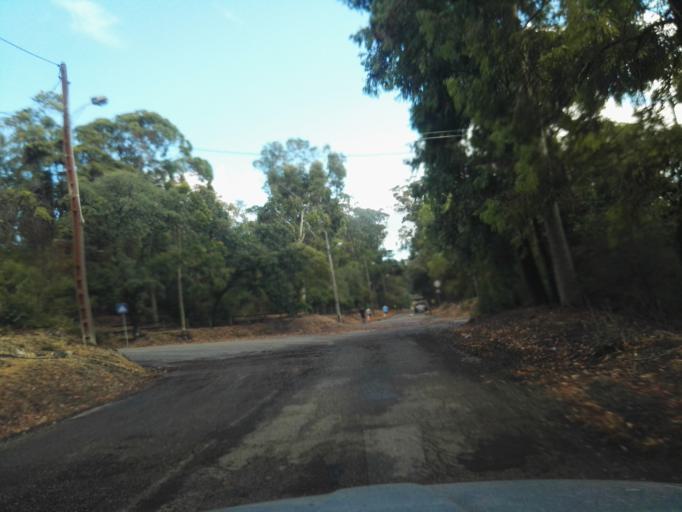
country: PT
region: Lisbon
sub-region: Oeiras
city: Alges
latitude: 38.7260
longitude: -9.1995
